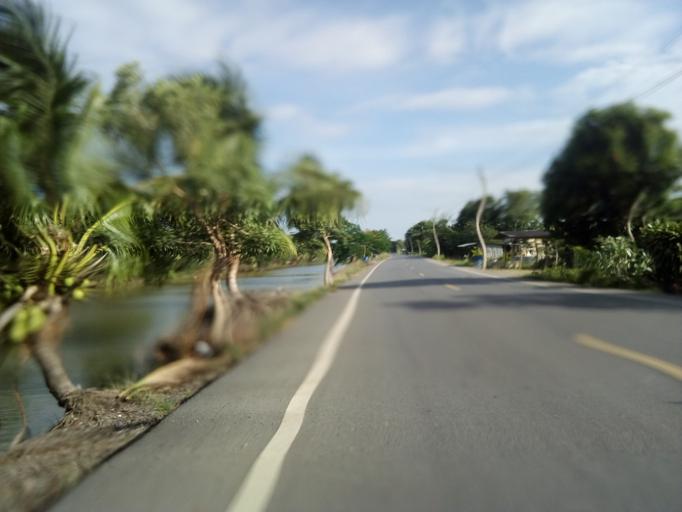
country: TH
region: Pathum Thani
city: Nong Suea
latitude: 14.1036
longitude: 100.8461
